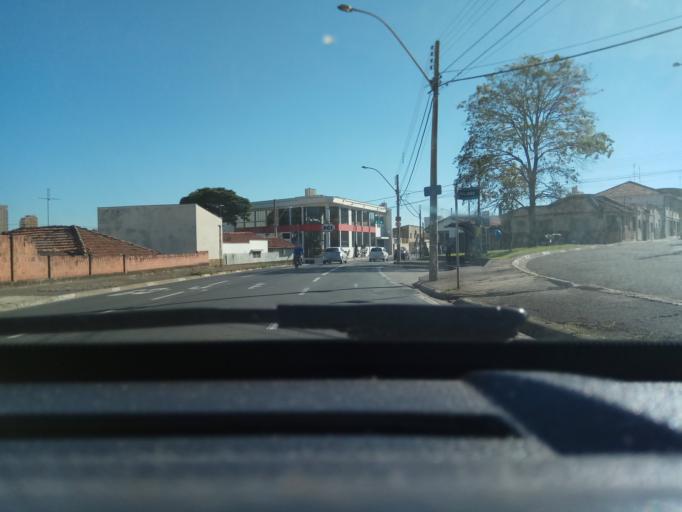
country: BR
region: Sao Paulo
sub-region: Piracicaba
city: Piracicaba
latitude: -22.7350
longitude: -47.6479
